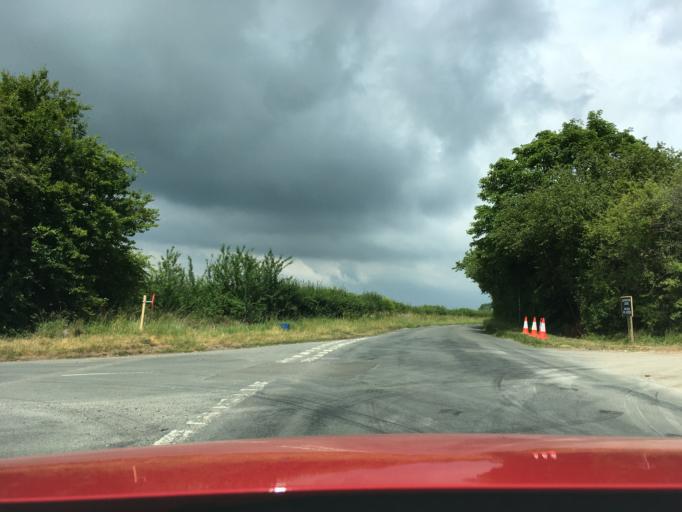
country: GB
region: England
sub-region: Gloucestershire
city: Coates
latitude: 51.7248
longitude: -2.0728
